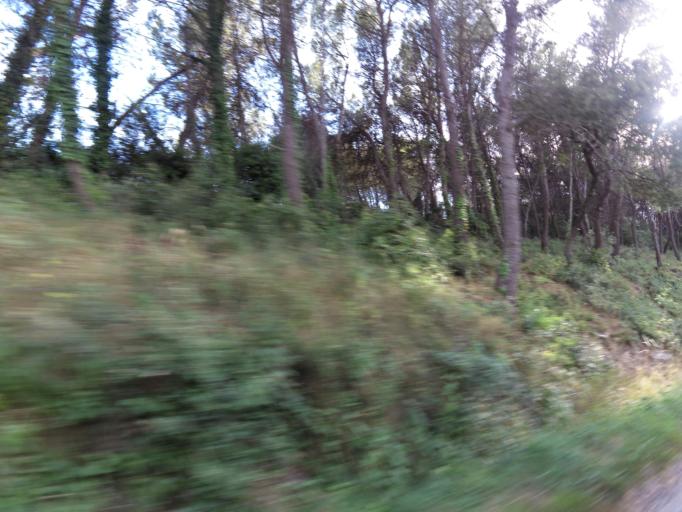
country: FR
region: Languedoc-Roussillon
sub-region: Departement du Gard
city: Congenies
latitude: 43.7880
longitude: 4.1723
